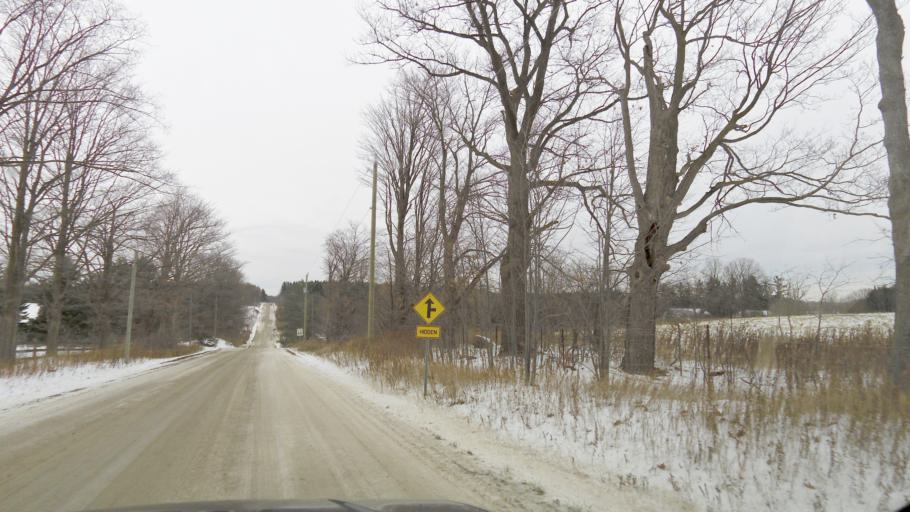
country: CA
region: Ontario
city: Vaughan
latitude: 43.9370
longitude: -79.6093
